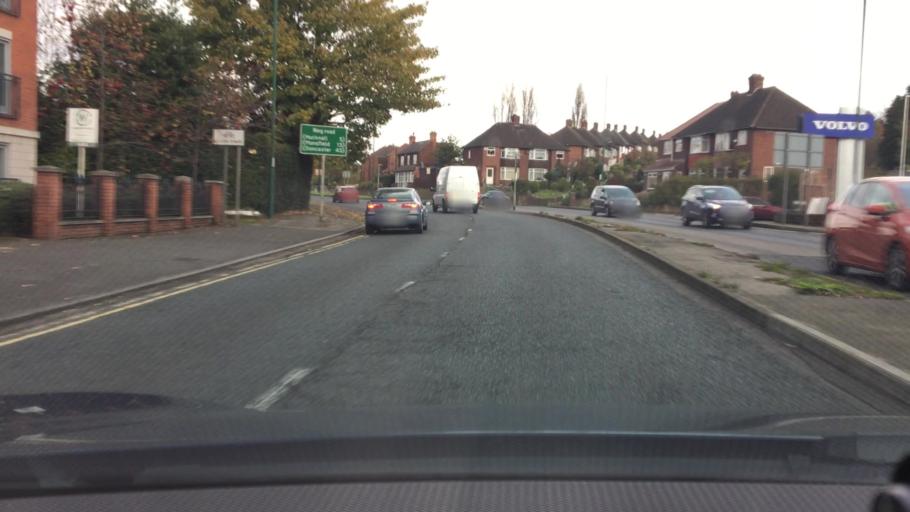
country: GB
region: England
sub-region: Nottingham
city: Nottingham
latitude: 52.9812
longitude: -1.1735
